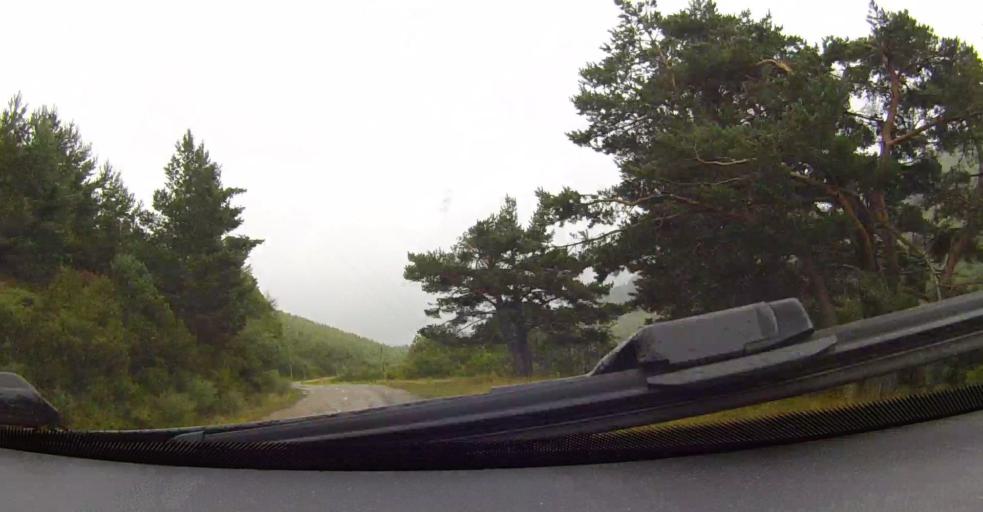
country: ES
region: Castille and Leon
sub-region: Provincia de Leon
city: Puebla de Lillo
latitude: 43.0746
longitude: -5.2556
